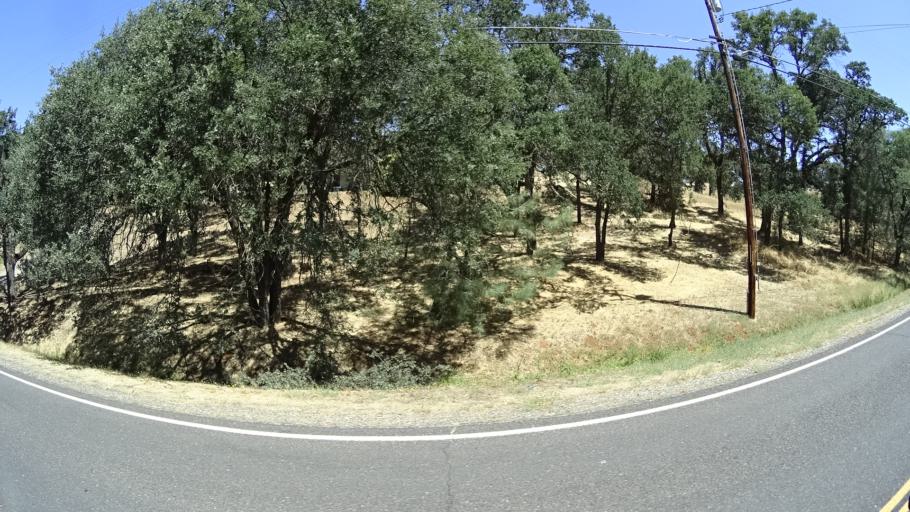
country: US
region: California
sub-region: Calaveras County
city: Rancho Calaveras
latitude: 38.1298
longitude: -120.8710
